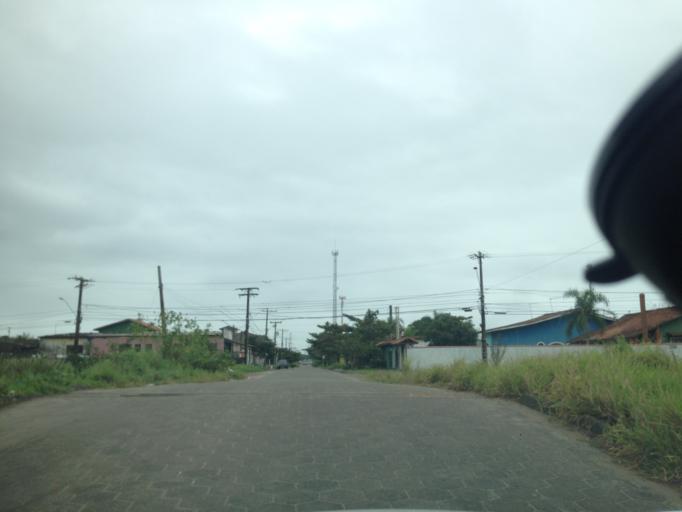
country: BR
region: Sao Paulo
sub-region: Itanhaem
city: Itanhaem
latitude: -24.2264
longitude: -46.8746
